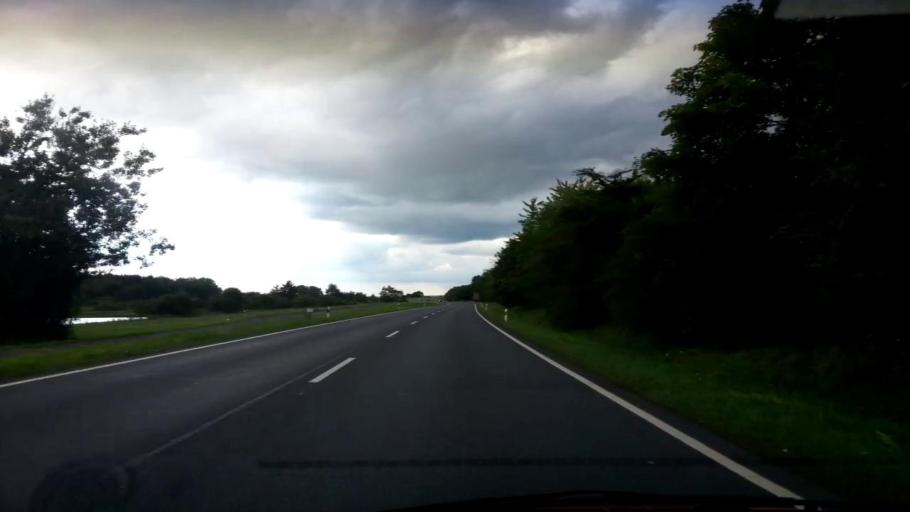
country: DE
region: Bavaria
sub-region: Regierungsbezirk Mittelfranken
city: Hemhofen
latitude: 49.7001
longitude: 10.9215
